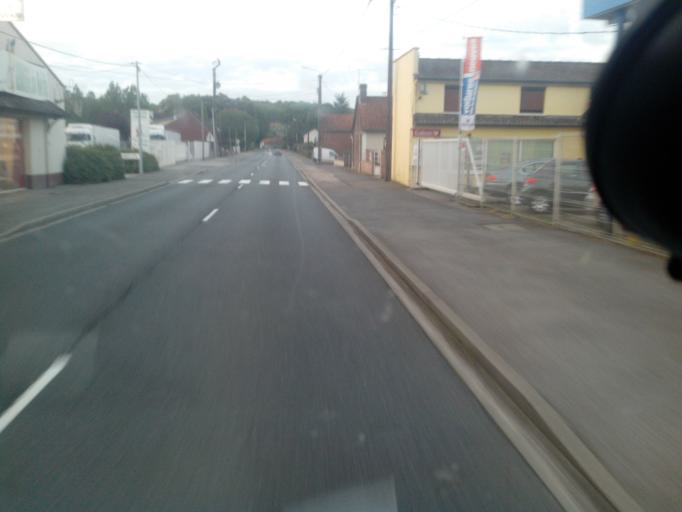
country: FR
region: Nord-Pas-de-Calais
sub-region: Departement du Pas-de-Calais
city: Marconnelle
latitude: 50.2732
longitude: 1.9853
